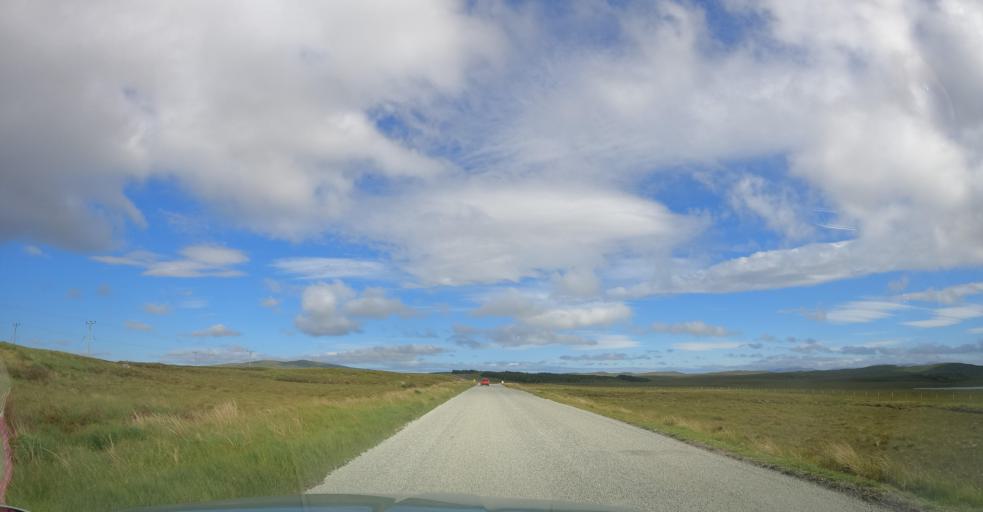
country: GB
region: Scotland
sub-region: Eilean Siar
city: Isle of Lewis
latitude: 58.1848
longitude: -6.6761
